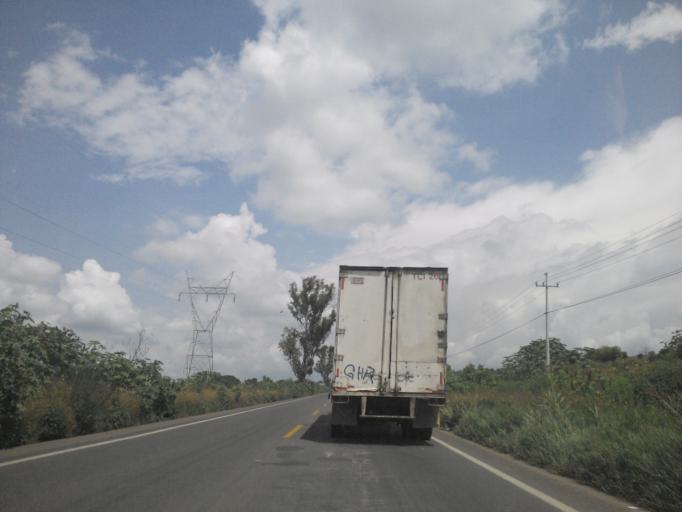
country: MX
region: Jalisco
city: Acatic
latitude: 20.7127
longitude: -102.9413
